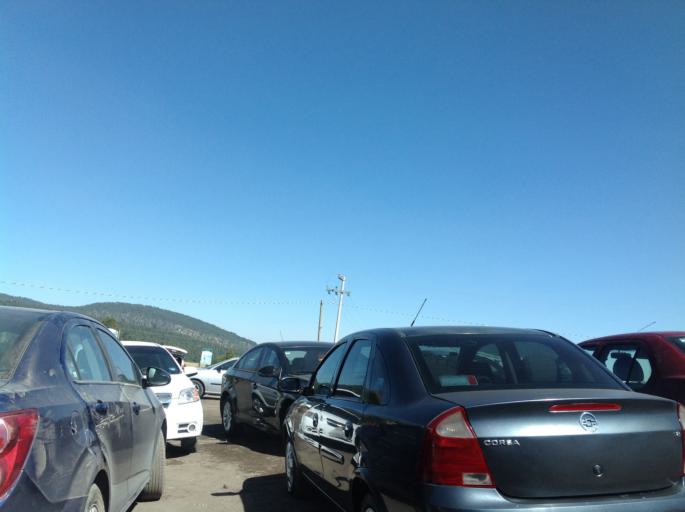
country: MX
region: Mexico
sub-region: Amecameca
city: San Diego Huehuecalco
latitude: 19.0867
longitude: -98.6470
